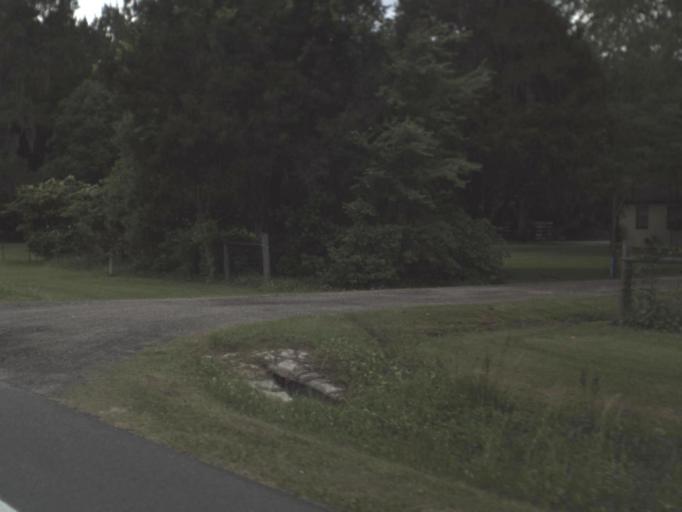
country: US
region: Florida
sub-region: Columbia County
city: Five Points
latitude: 30.3978
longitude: -82.6310
